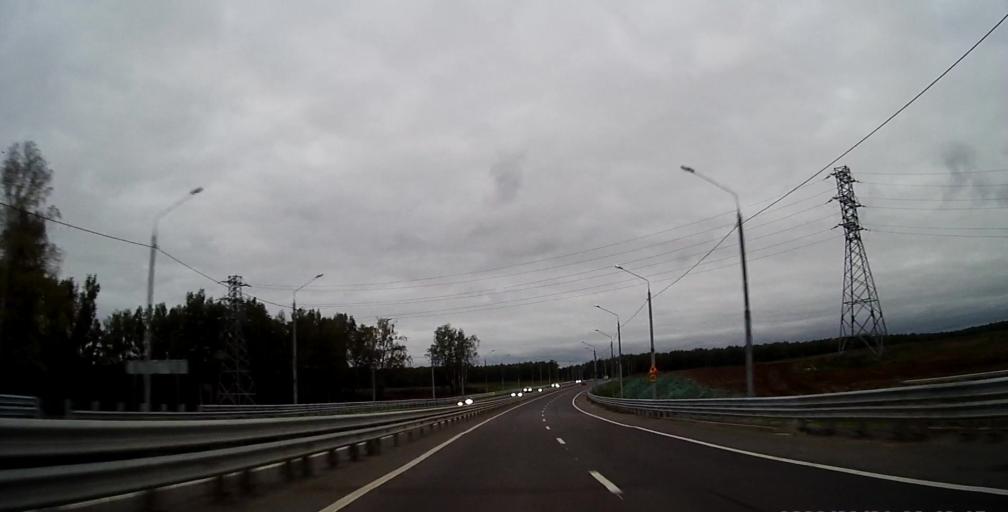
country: RU
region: Moskovskaya
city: Klimovsk
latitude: 55.3957
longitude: 37.5022
